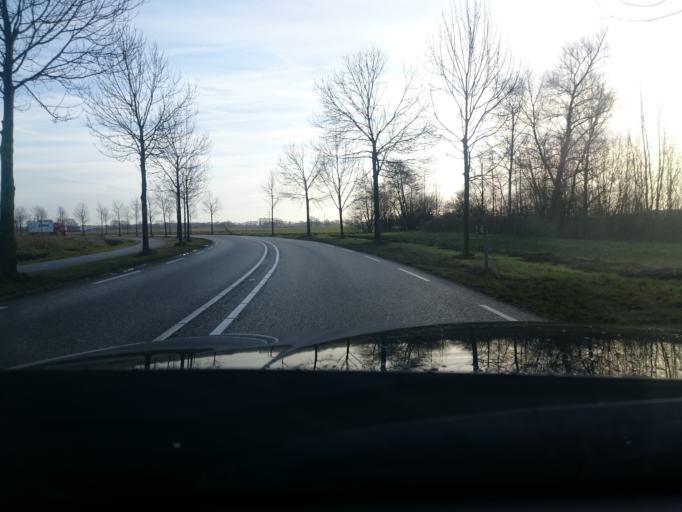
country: NL
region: Overijssel
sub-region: Gemeente Raalte
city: Raalte
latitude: 52.3694
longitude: 6.2808
